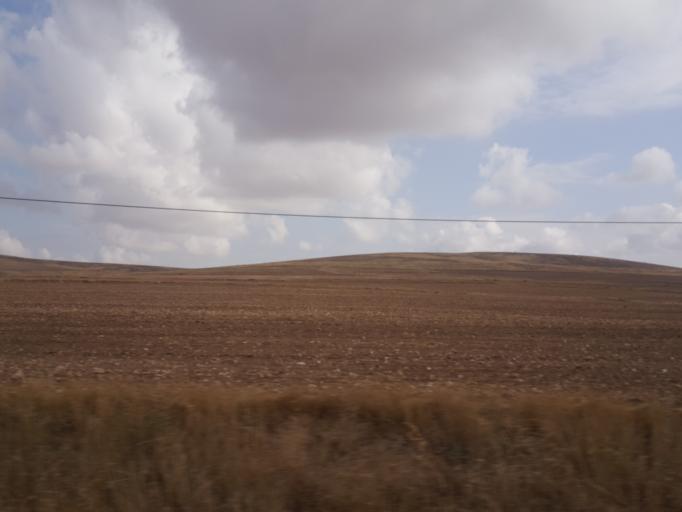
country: TR
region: Kirikkale
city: Keskin
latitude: 39.6304
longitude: 33.6098
